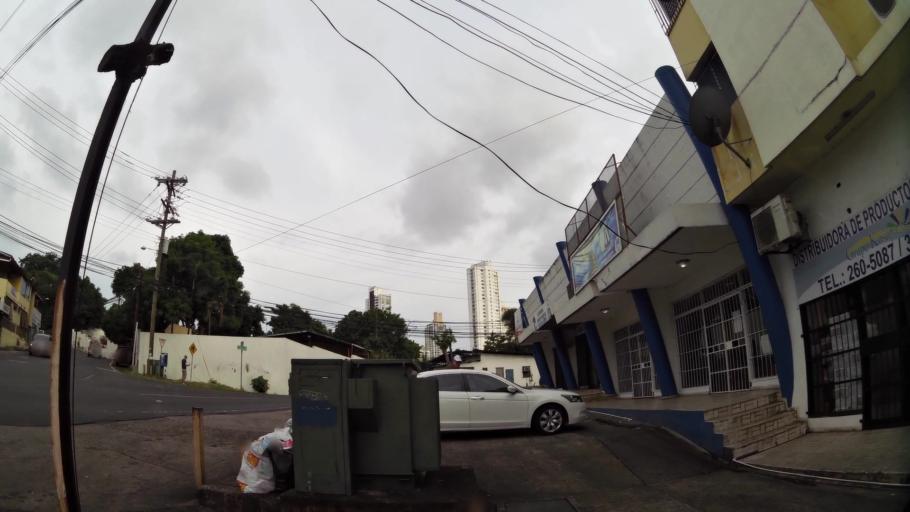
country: PA
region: Panama
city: Panama
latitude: 8.9966
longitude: -79.5166
